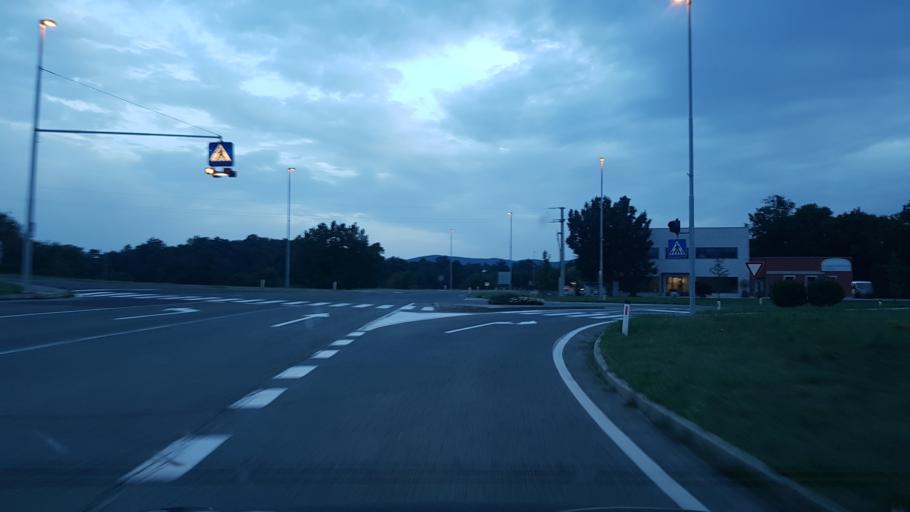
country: SI
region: Divaca
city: Divaca
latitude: 45.6796
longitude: 13.9718
